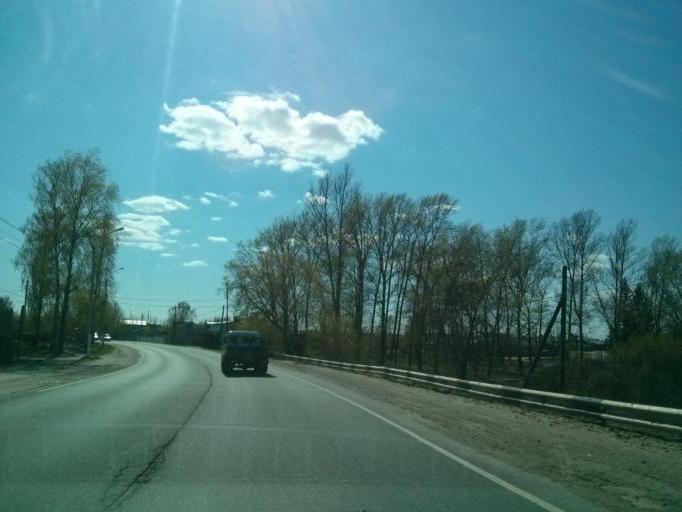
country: RU
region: Nizjnij Novgorod
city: Taremskoye
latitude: 55.9298
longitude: 43.0410
